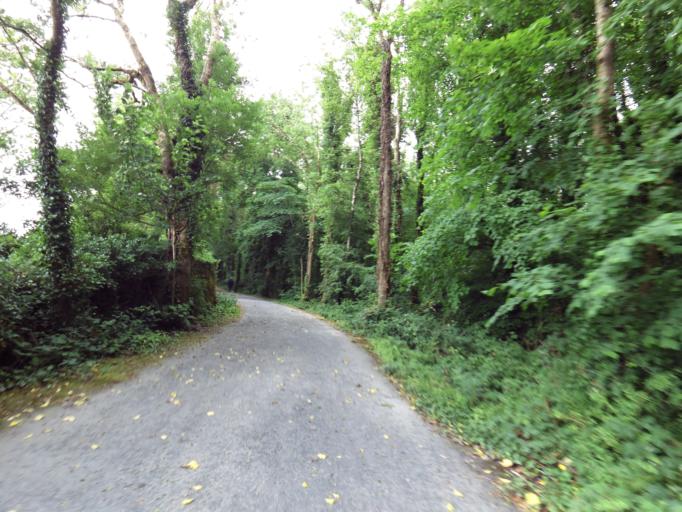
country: IE
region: Connaught
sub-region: County Galway
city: Gort
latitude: 53.0852
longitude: -8.8419
